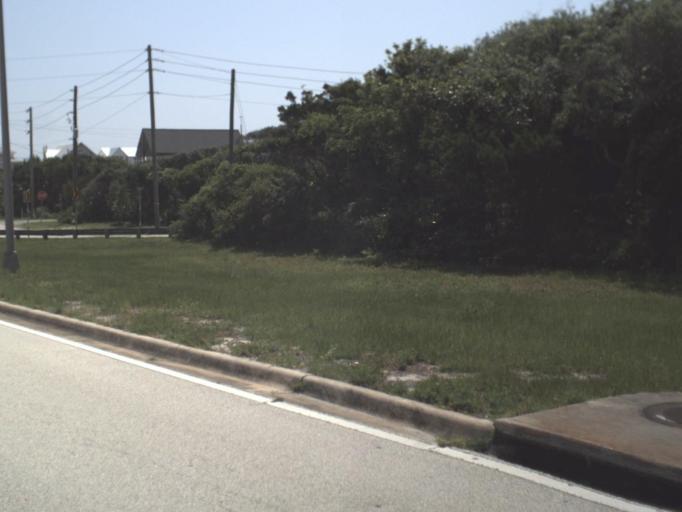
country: US
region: Florida
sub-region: Saint Johns County
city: Butler Beach
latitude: 29.7702
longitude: -81.2560
